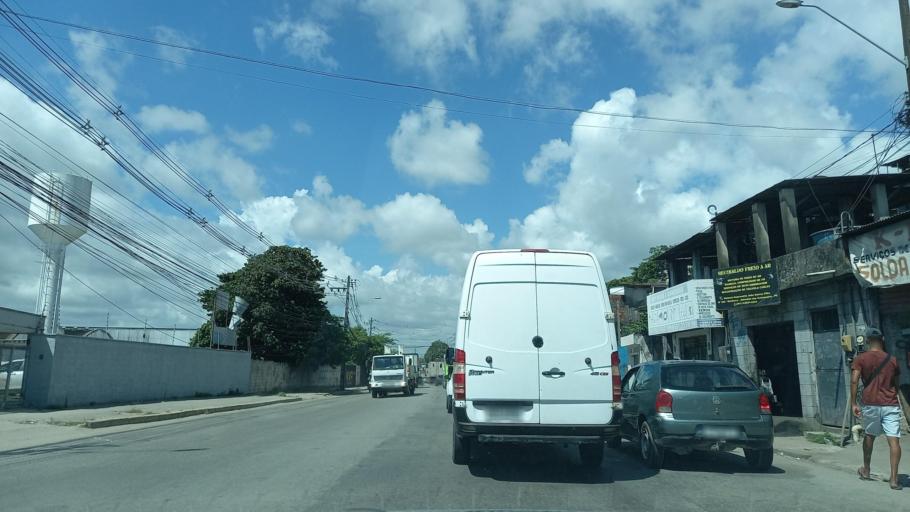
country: BR
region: Pernambuco
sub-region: Jaboatao Dos Guararapes
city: Jaboatao
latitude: -8.1545
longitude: -34.9431
